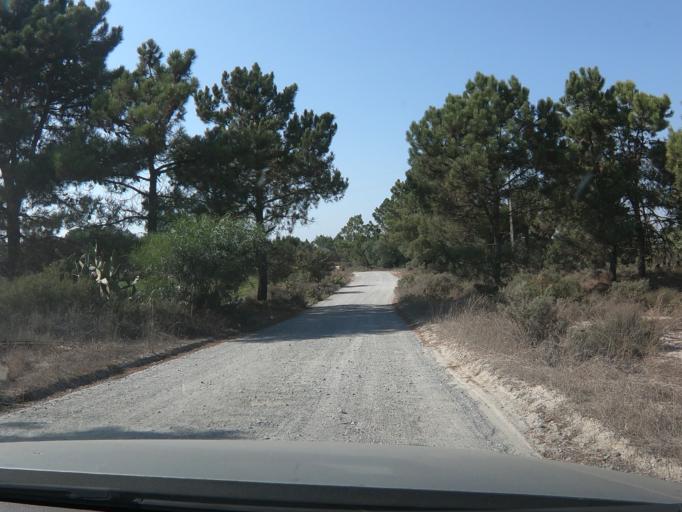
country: PT
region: Setubal
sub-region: Setubal
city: Setubal
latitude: 38.3951
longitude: -8.7795
